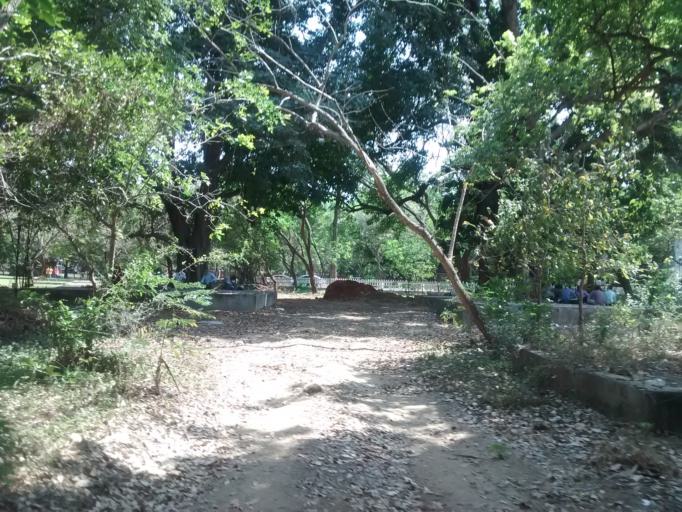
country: IN
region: Tamil Nadu
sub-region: Chennai
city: Gandhi Nagar
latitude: 13.0097
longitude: 80.2345
